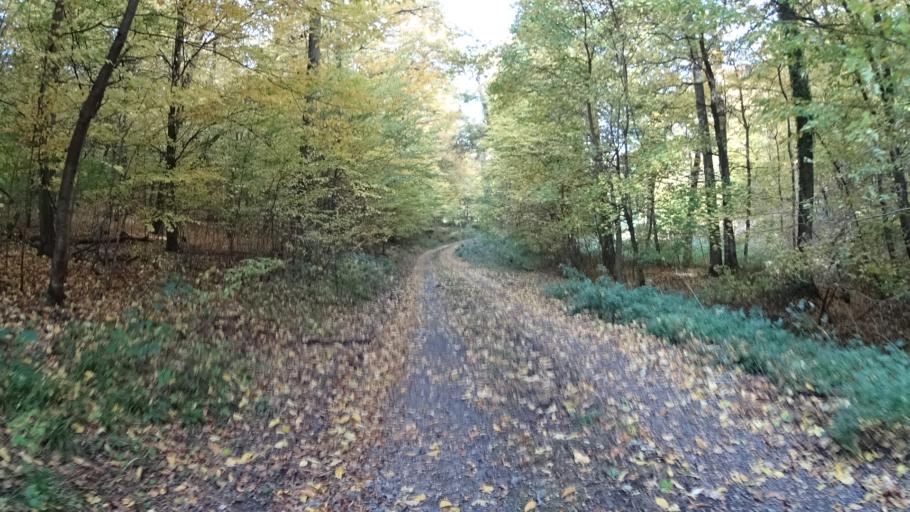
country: DE
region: Rheinland-Pfalz
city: Stein-Bockenheim
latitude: 49.7548
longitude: 7.9637
